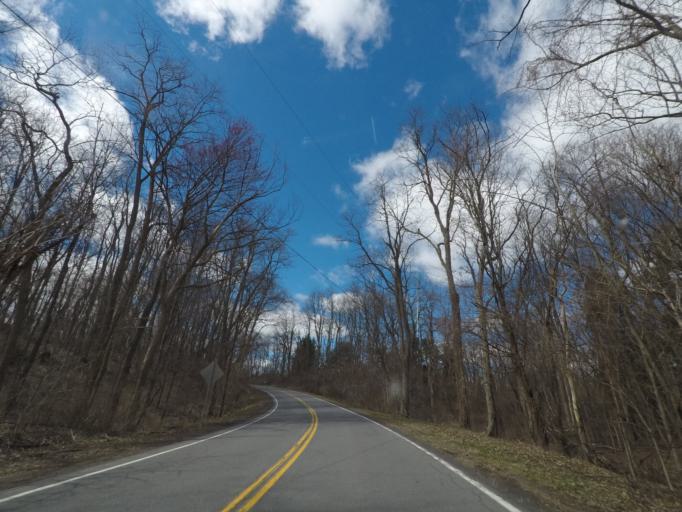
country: US
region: New York
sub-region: Albany County
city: Voorheesville
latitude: 42.6571
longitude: -73.9883
